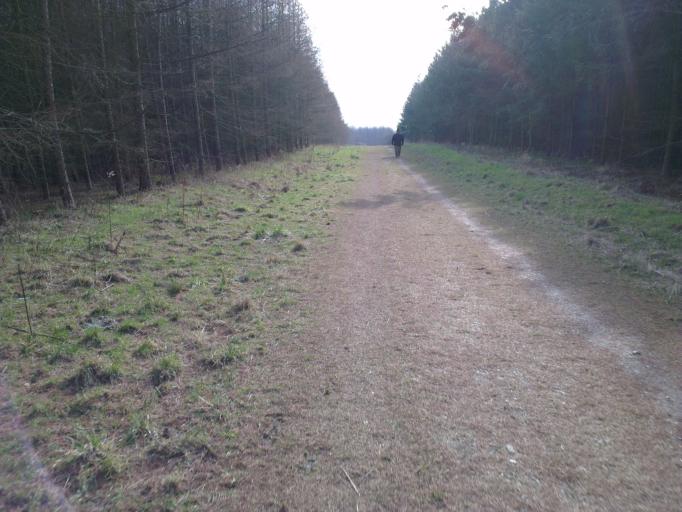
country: DK
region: Capital Region
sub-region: Frederikssund Kommune
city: Frederikssund
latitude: 55.8397
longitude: 12.0891
